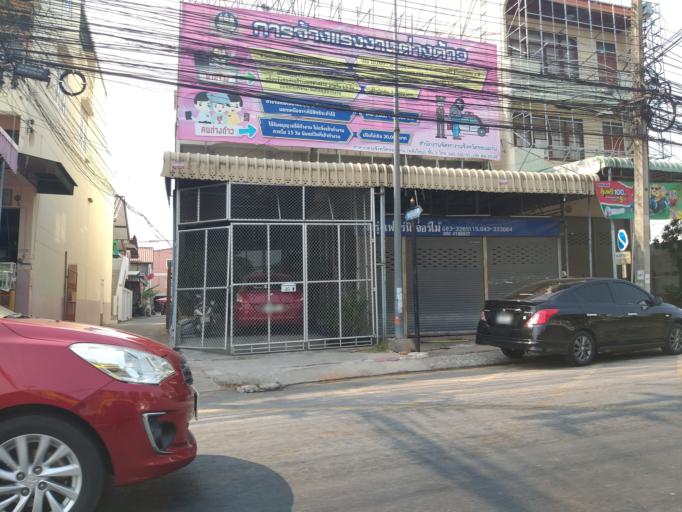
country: TH
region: Khon Kaen
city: Khon Kaen
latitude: 16.4408
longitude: 102.8309
